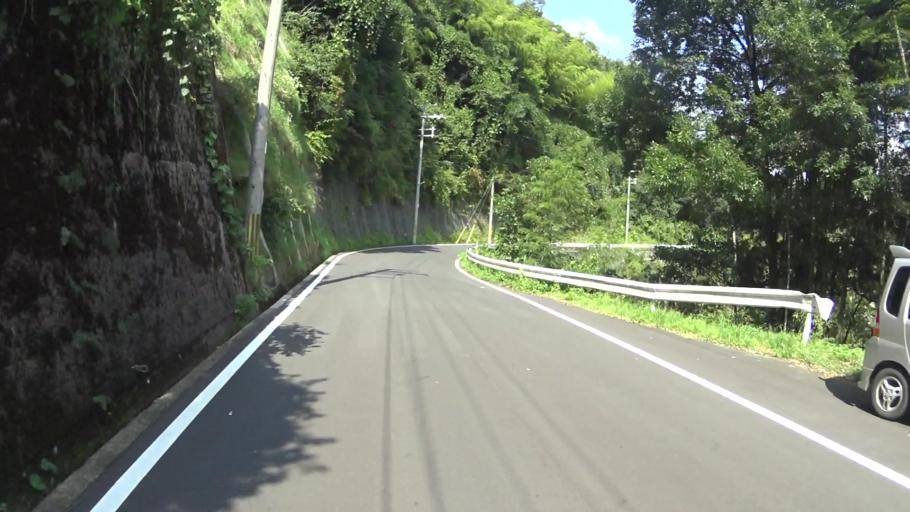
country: JP
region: Kyoto
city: Miyazu
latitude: 35.6300
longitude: 135.2321
